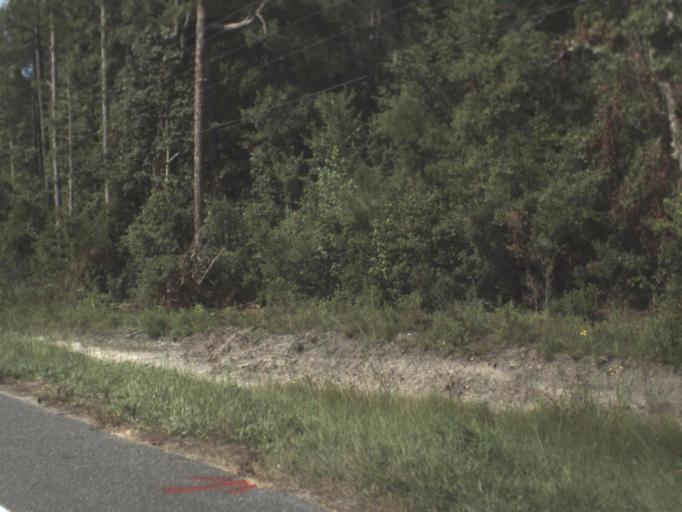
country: US
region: Florida
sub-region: Taylor County
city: Perry
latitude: 30.2436
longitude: -83.6206
